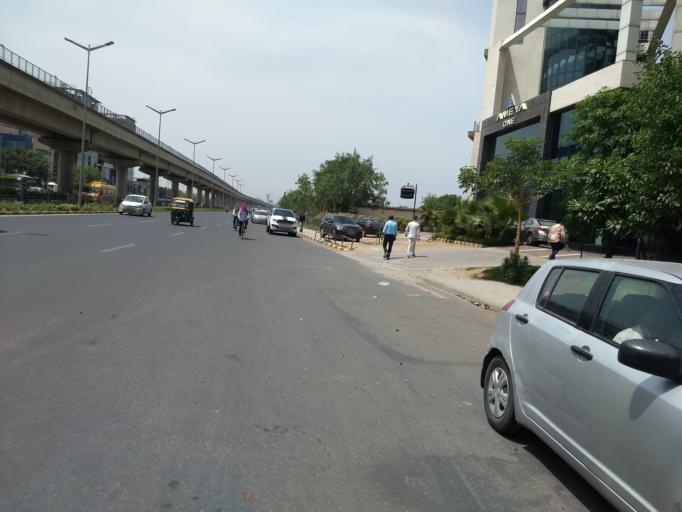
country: IN
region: Haryana
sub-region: Gurgaon
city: Gurgaon
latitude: 28.4581
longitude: 77.0971
